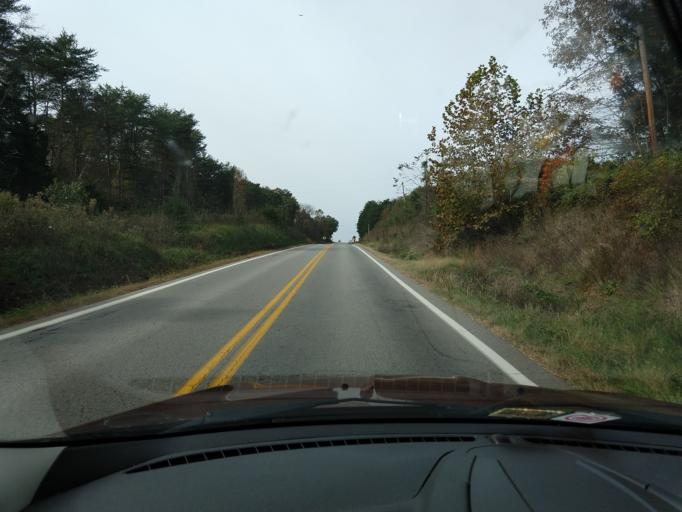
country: US
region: Virginia
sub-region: Pittsylvania County
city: Gretna
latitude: 36.9441
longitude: -79.4930
